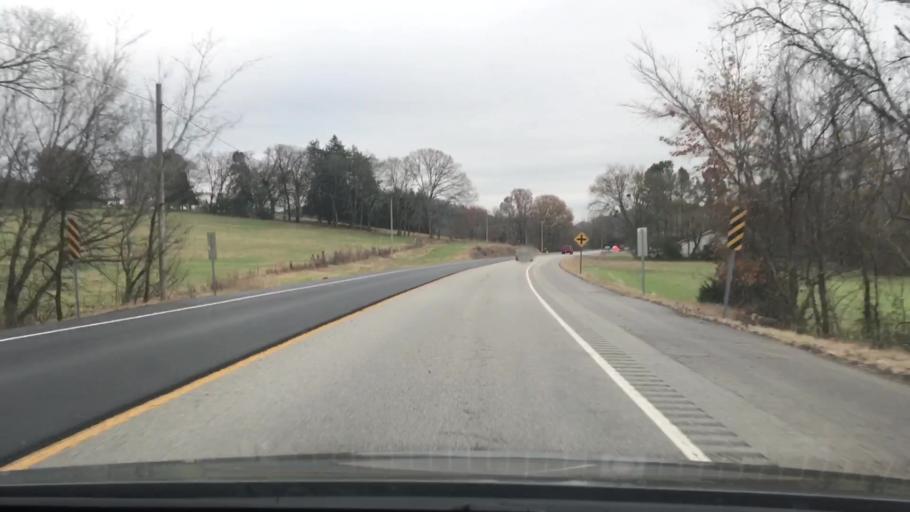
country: US
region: Tennessee
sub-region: Smith County
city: Carthage
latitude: 36.3173
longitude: -86.0110
